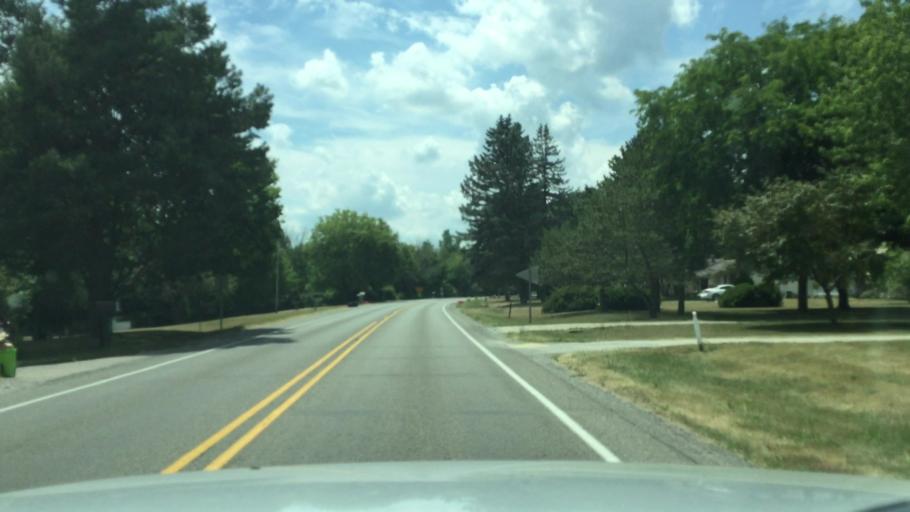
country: US
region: Michigan
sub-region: Genesee County
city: Flushing
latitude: 43.0865
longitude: -83.8666
